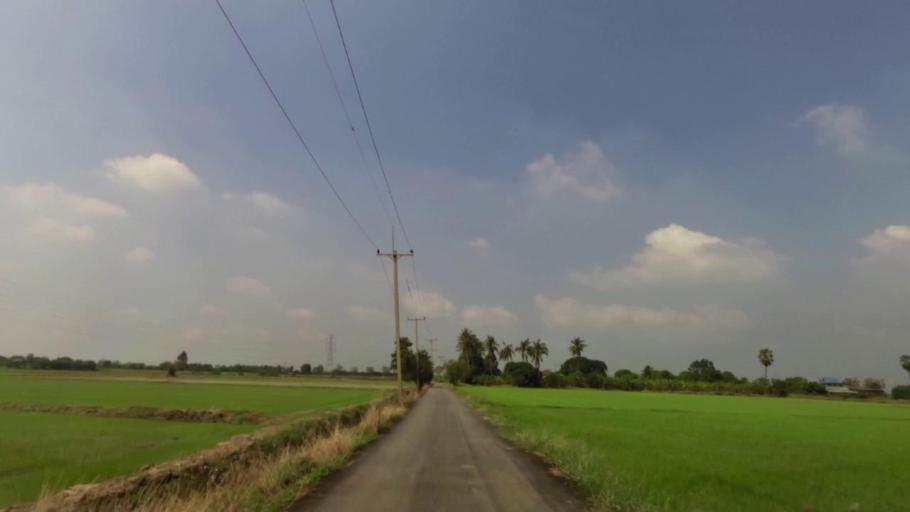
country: TH
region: Ang Thong
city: Pho Thong
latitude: 14.6198
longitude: 100.4007
